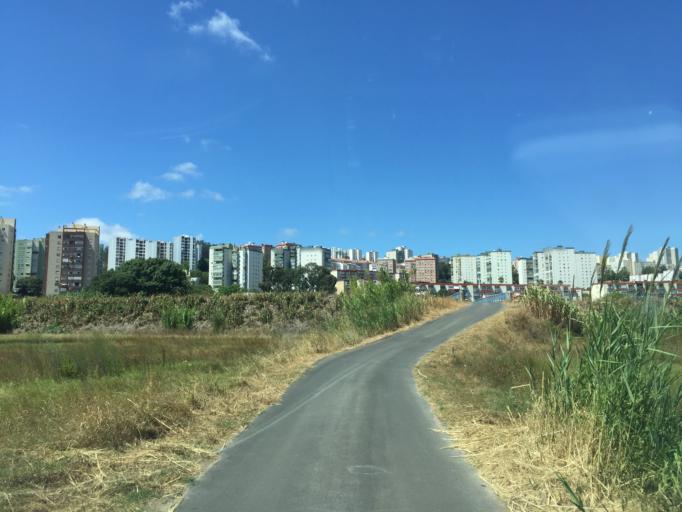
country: PT
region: Lisbon
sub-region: Odivelas
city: Povoa de Santo Adriao
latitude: 38.8088
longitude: -9.1541
